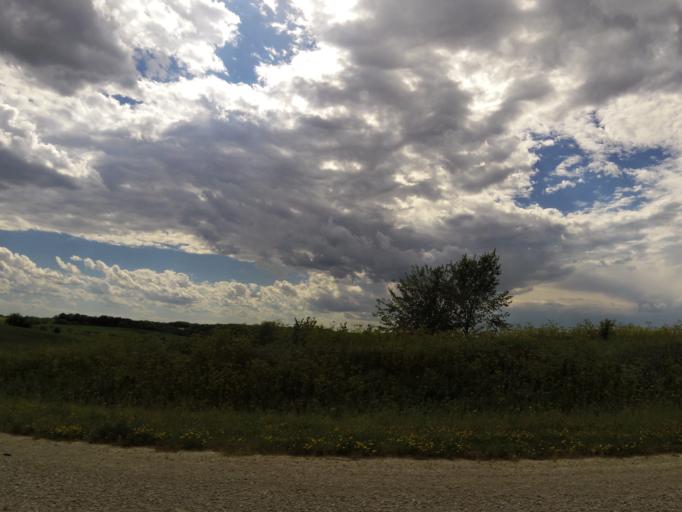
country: US
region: Iowa
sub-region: Henry County
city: Mount Pleasant
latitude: 40.8695
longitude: -91.5654
